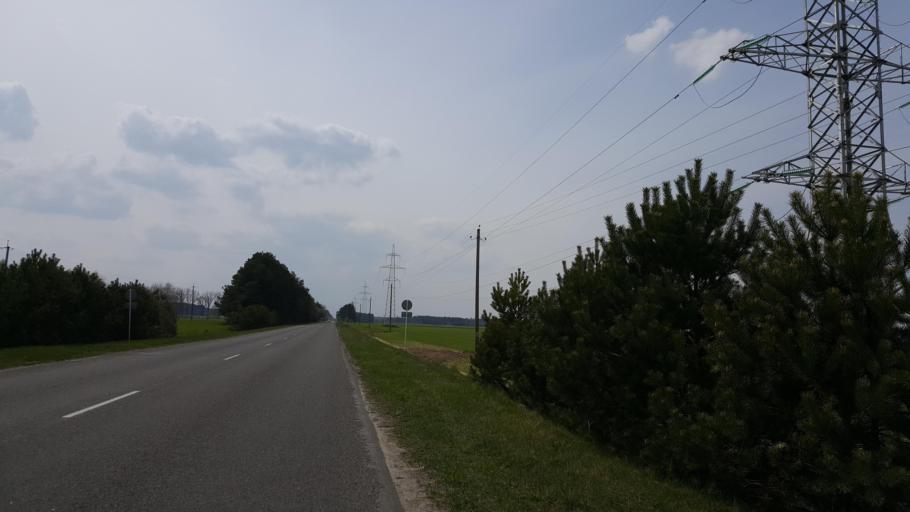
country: BY
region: Brest
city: Zhabinka
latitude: 52.2093
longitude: 23.9548
